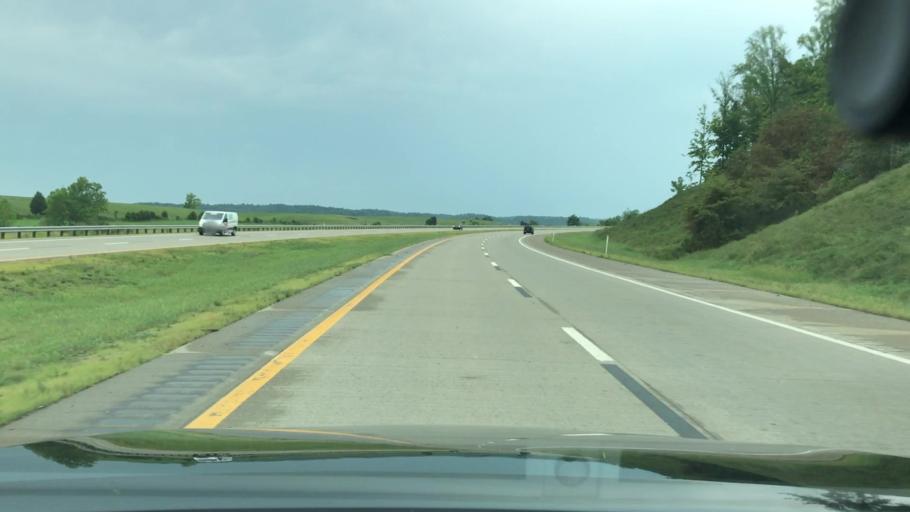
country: US
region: West Virginia
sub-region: Mason County
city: Point Pleasant
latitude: 38.7711
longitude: -82.0469
